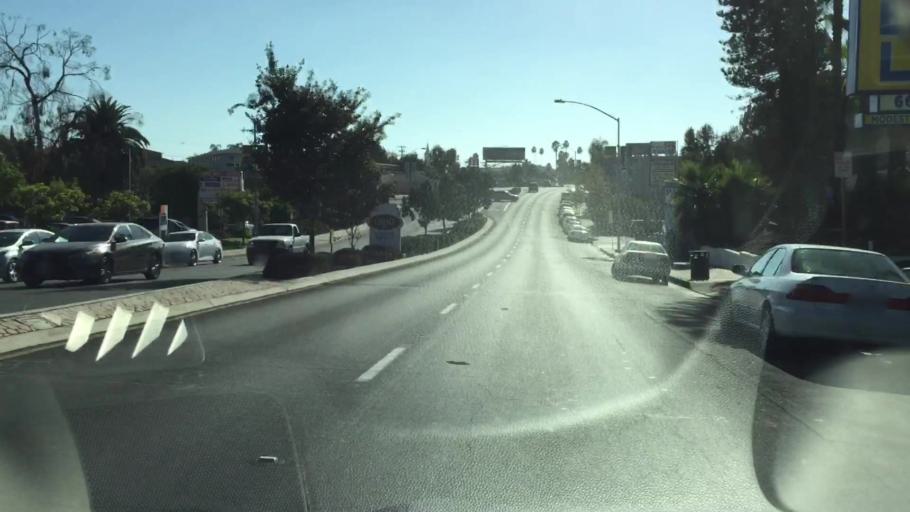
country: US
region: California
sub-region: San Diego County
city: La Mesa
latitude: 32.7680
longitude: -117.0551
